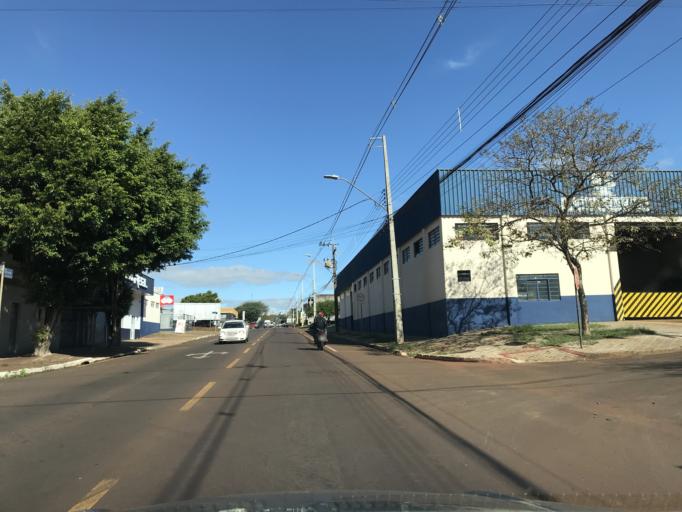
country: BR
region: Parana
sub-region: Cascavel
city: Cascavel
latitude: -24.9318
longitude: -53.4751
